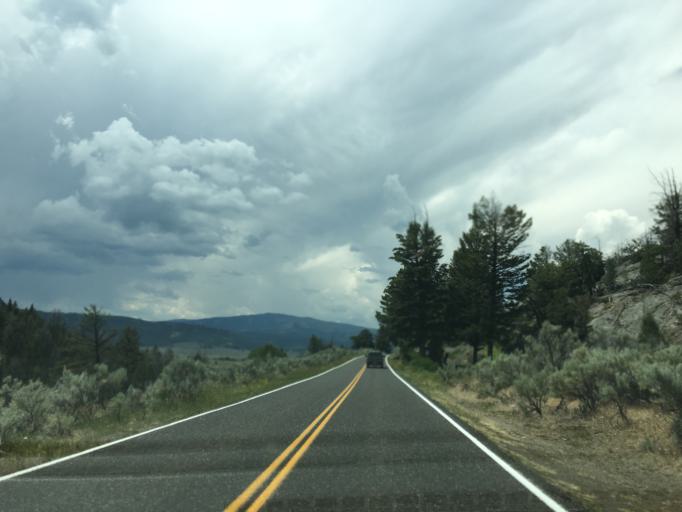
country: US
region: Montana
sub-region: Park County
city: Livingston
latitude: 44.9196
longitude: -110.2983
